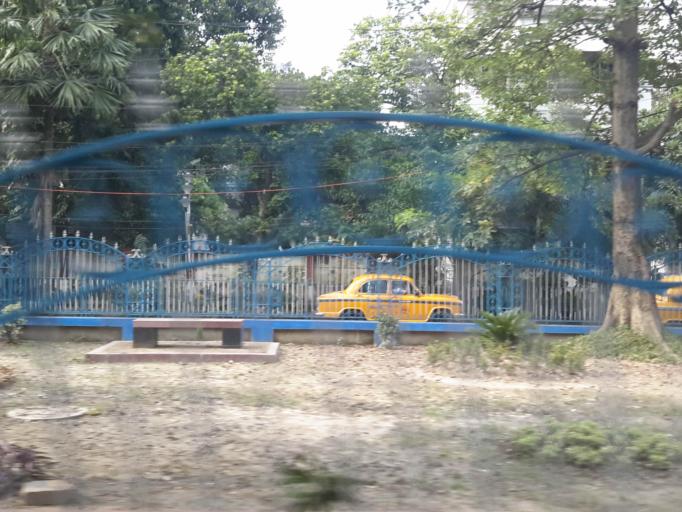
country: IN
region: West Bengal
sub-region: Kolkata
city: Kolkata
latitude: 22.5142
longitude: 88.3640
